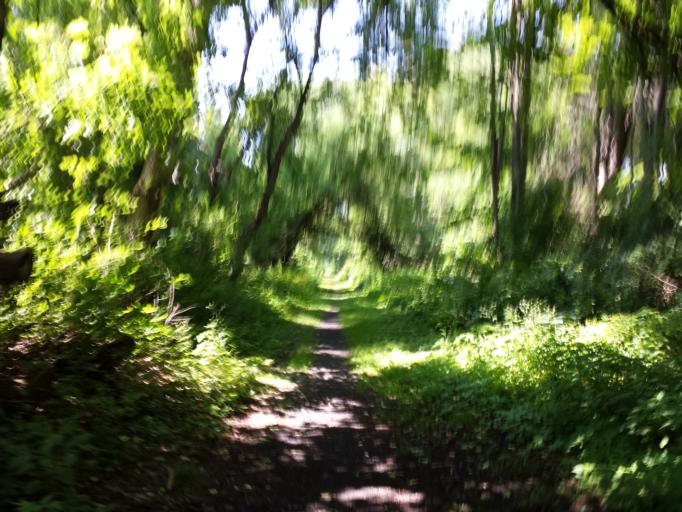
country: US
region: Vermont
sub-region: Rutland County
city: Castleton
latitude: 43.6117
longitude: -73.1736
